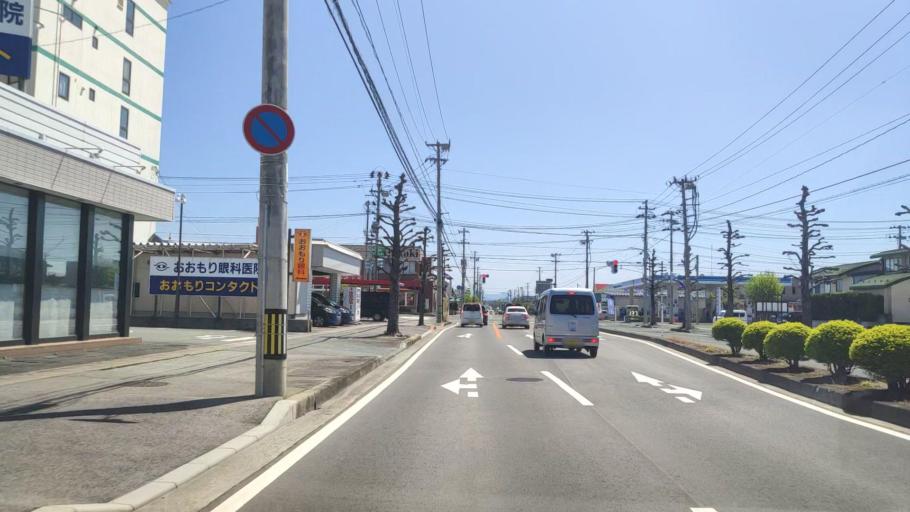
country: JP
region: Yamagata
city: Tendo
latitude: 38.3668
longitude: 140.3674
